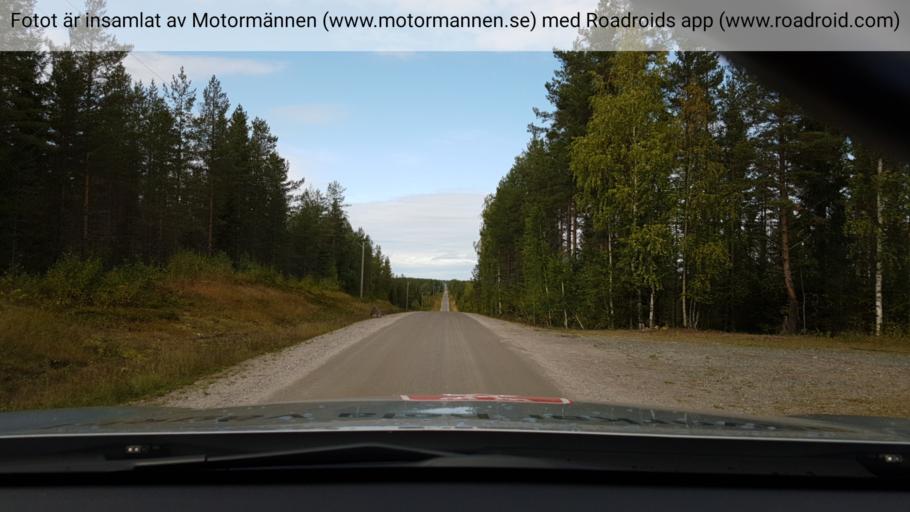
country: SE
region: Norrbotten
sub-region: Pitea Kommun
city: Roknas
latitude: 65.1622
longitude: 21.1458
